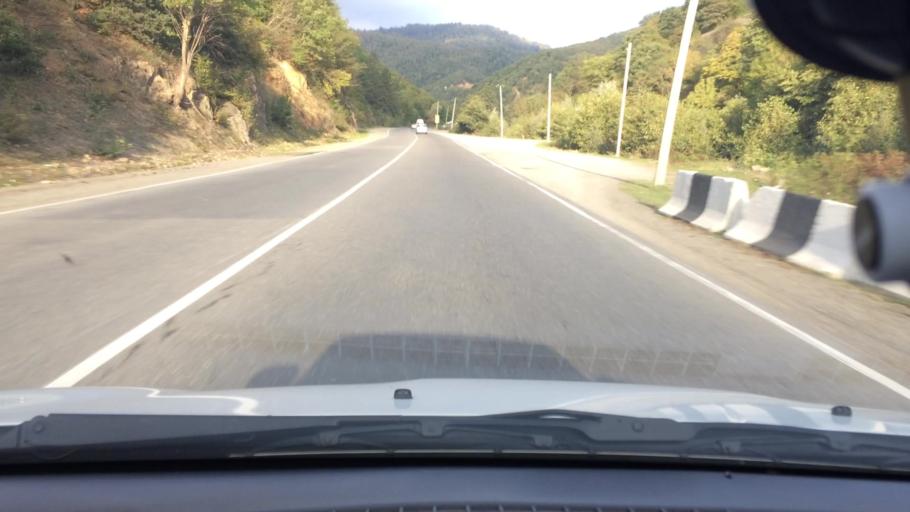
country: GE
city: Surami
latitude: 42.0382
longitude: 43.5163
